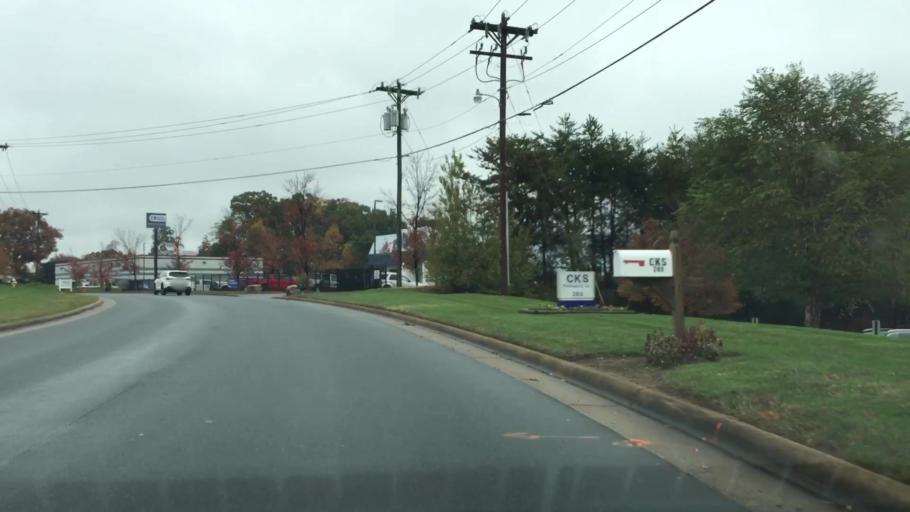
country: US
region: North Carolina
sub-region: Iredell County
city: Mooresville
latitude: 35.5842
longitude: -80.8602
